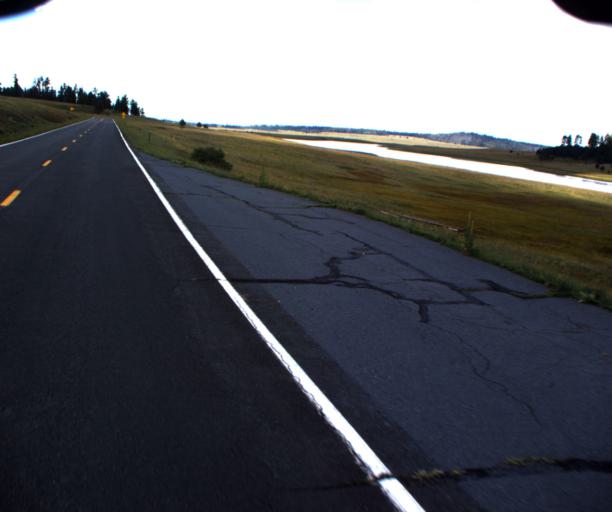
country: US
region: Arizona
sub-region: Apache County
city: Eagar
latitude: 33.9102
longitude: -109.4141
